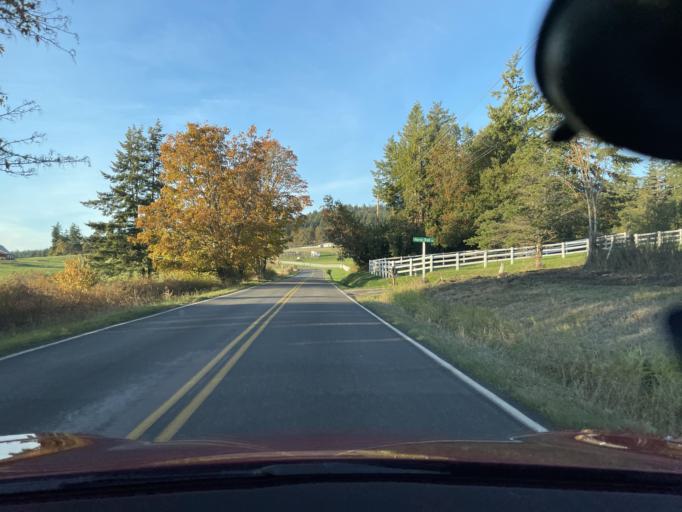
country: US
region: Washington
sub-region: San Juan County
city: Friday Harbor
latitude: 48.5717
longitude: -123.1390
